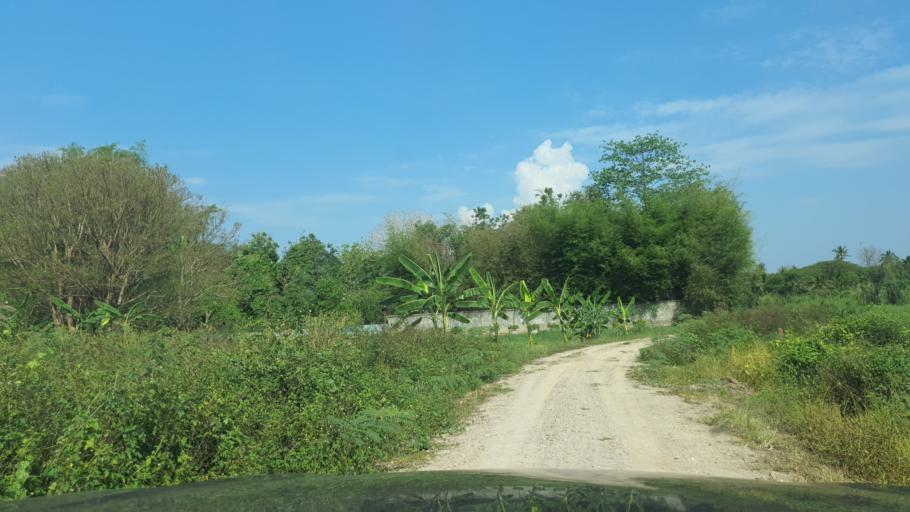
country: TH
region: Chiang Mai
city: Saraphi
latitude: 18.7292
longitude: 99.0453
